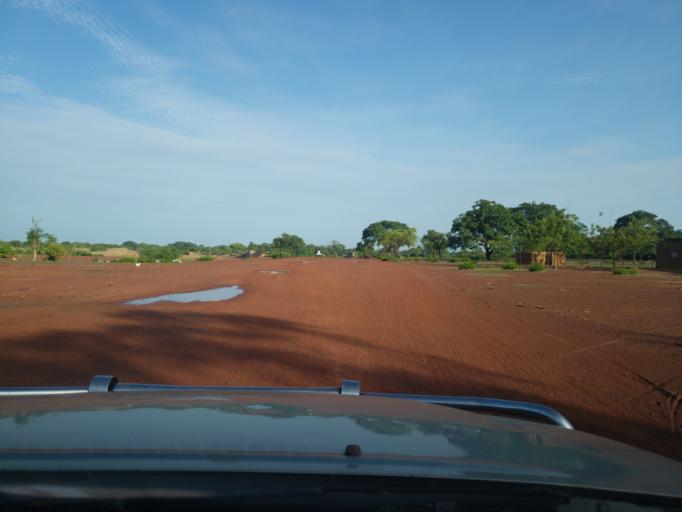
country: ML
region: Sikasso
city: Koutiala
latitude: 12.4193
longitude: -5.5787
